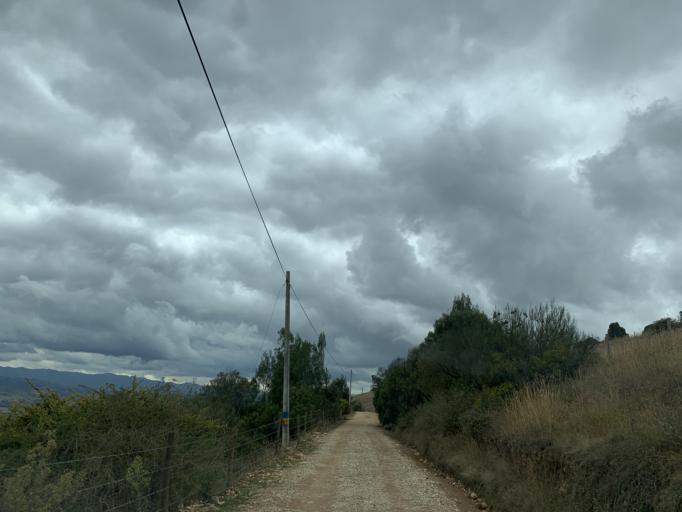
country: CO
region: Boyaca
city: Tunja
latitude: 5.5489
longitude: -73.3190
